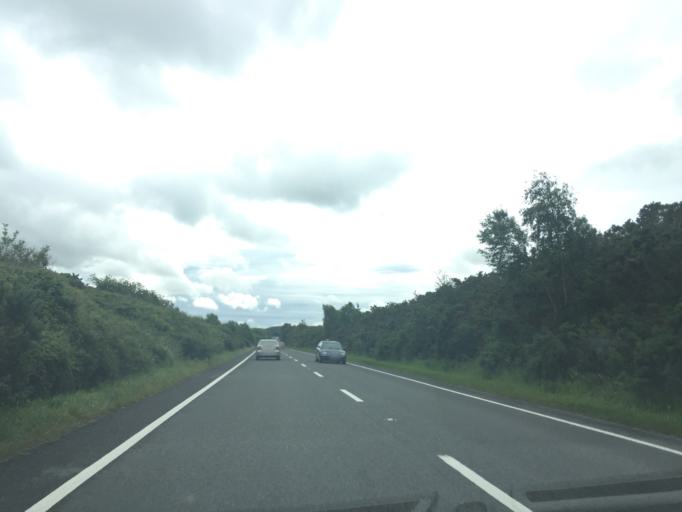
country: GB
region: England
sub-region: Dorset
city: Wareham
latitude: 50.6624
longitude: -2.0947
